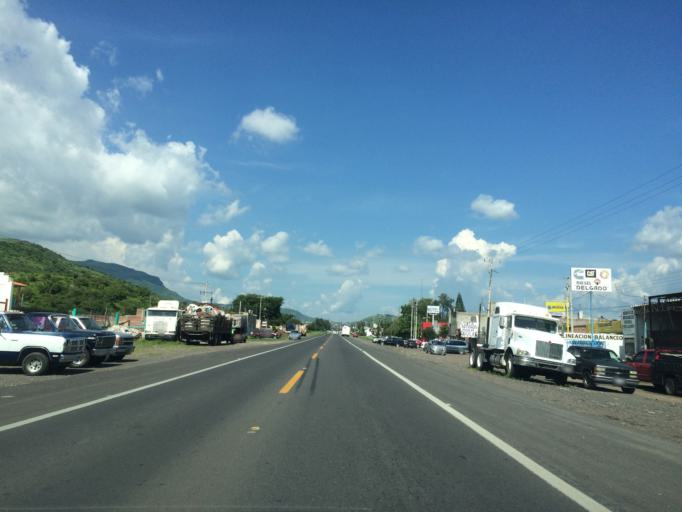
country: MX
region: Nayarit
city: Ixtlan del Rio
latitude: 21.0368
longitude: -104.4001
